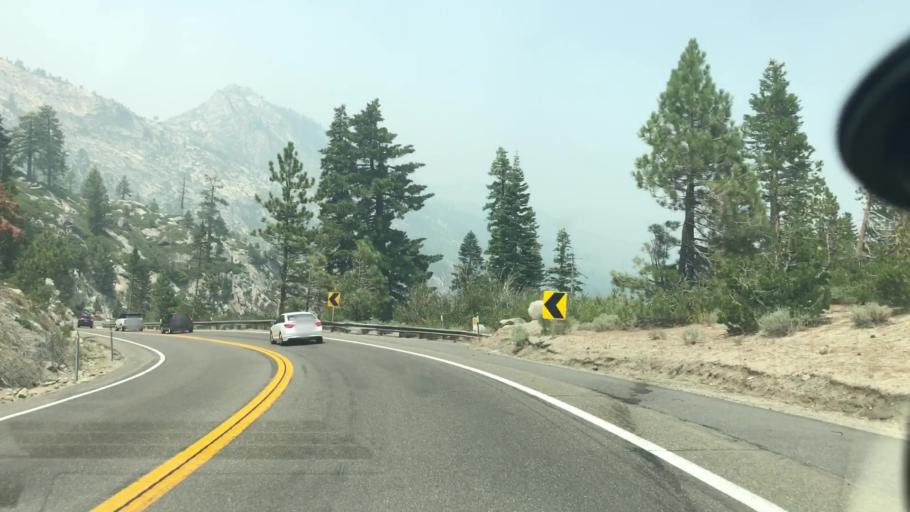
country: US
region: California
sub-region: El Dorado County
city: South Lake Tahoe
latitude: 38.8359
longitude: -120.0349
